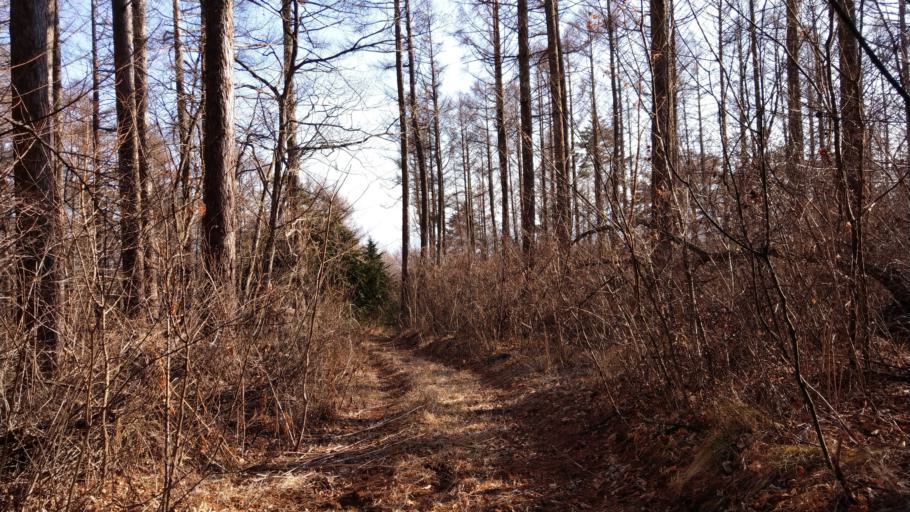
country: JP
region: Nagano
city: Komoro
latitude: 36.3669
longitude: 138.4311
